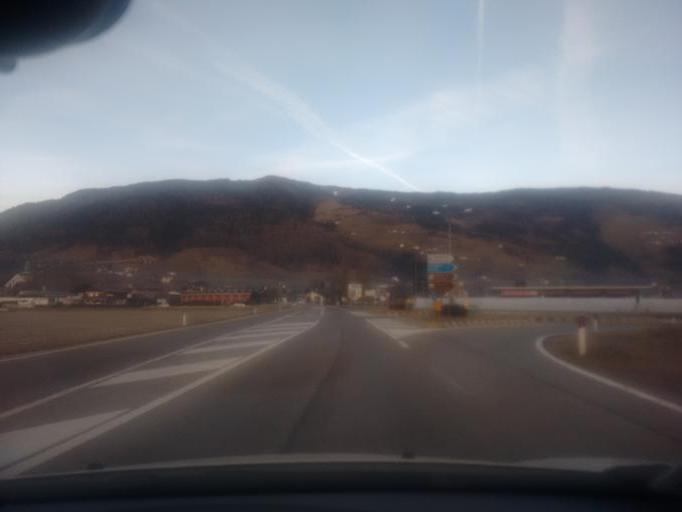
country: IT
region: Trentino-Alto Adige
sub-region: Bolzano
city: Vipiteno
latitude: 46.8899
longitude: 11.4388
